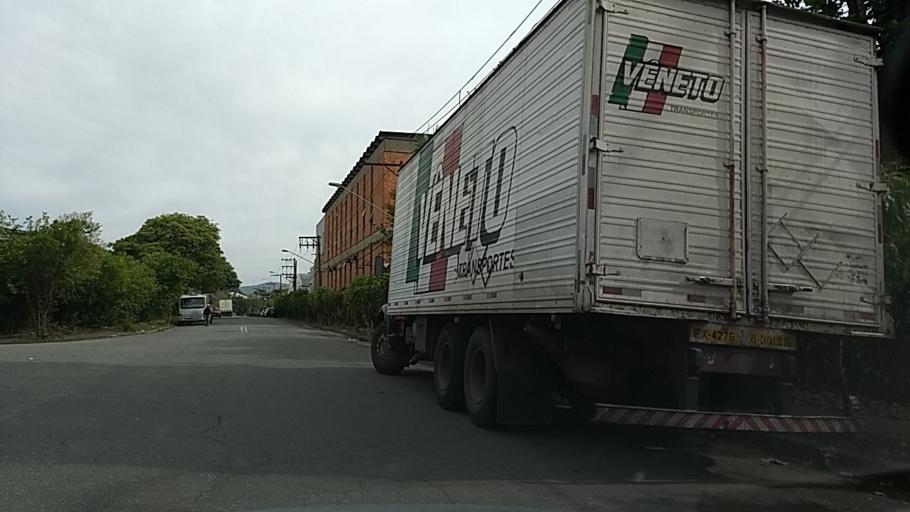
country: BR
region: Sao Paulo
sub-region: Guarulhos
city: Guarulhos
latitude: -23.5000
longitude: -46.5657
